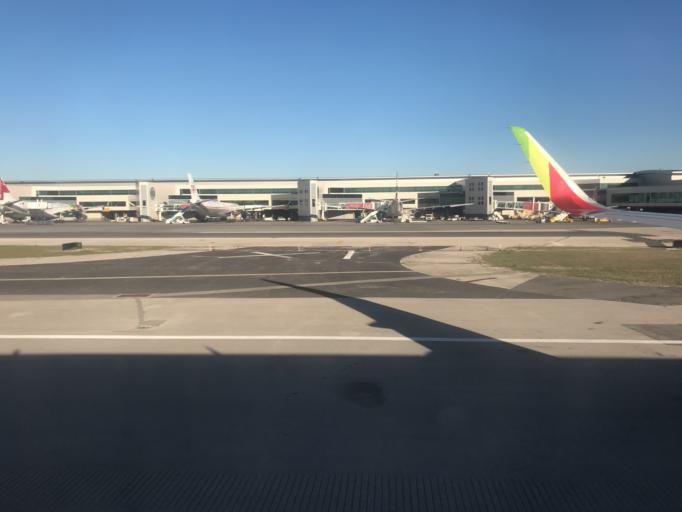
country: PT
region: Lisbon
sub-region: Loures
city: Camarate
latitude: 38.7739
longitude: -9.1338
